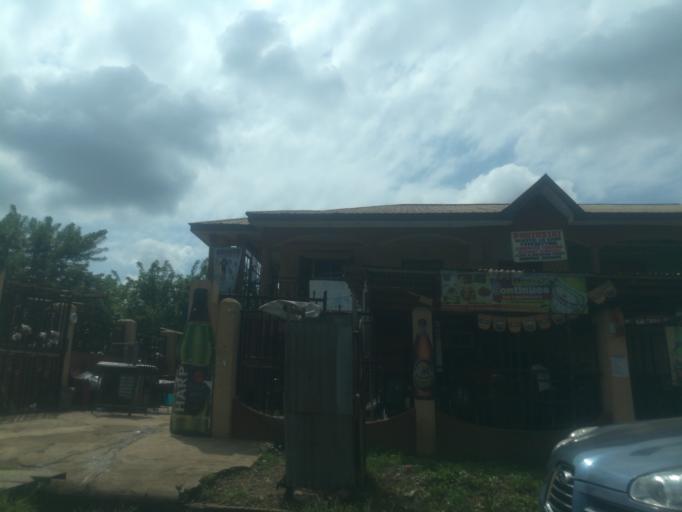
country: NG
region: Oyo
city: Egbeda
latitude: 7.4247
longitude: 3.9879
